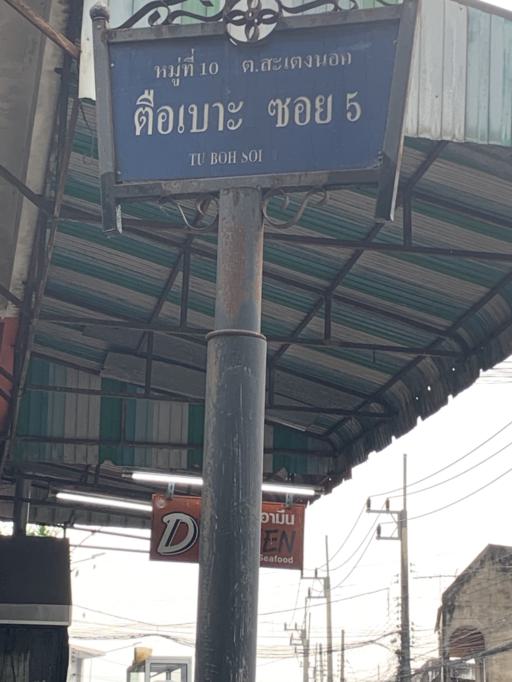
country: TH
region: Yala
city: Yala
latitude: 6.5412
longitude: 101.2932
